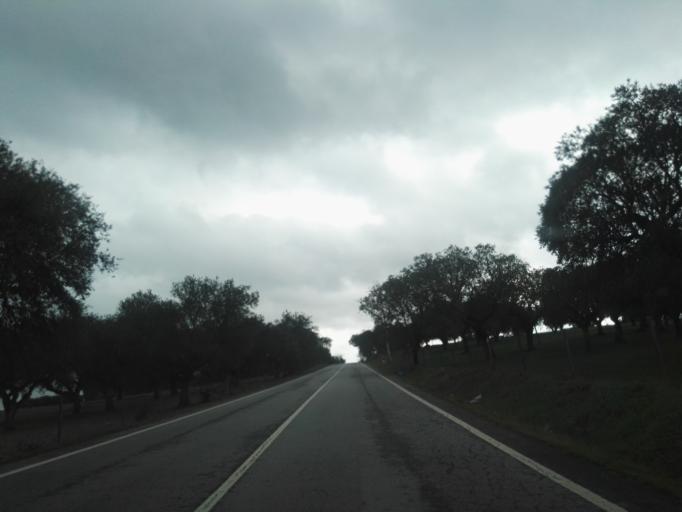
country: PT
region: Portalegre
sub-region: Arronches
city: Arronches
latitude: 39.1117
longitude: -7.2825
